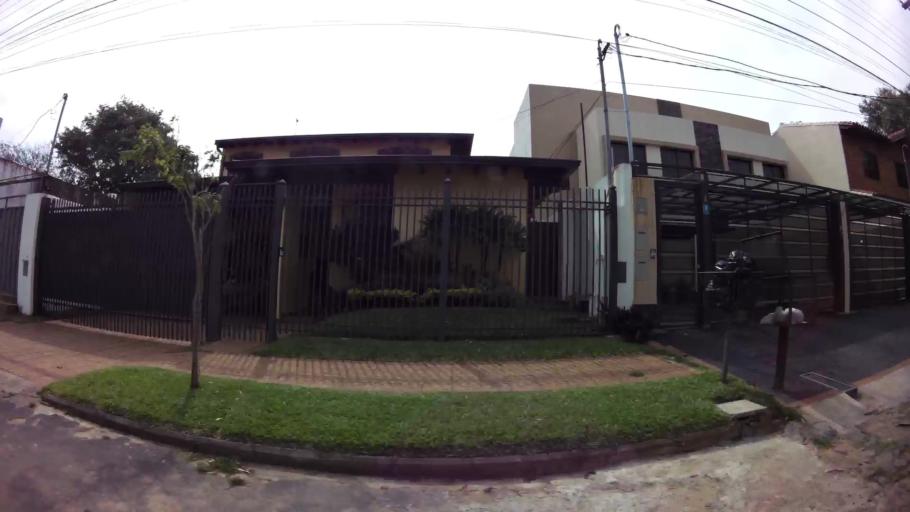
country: PY
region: Central
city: Fernando de la Mora
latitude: -25.2748
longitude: -57.5551
